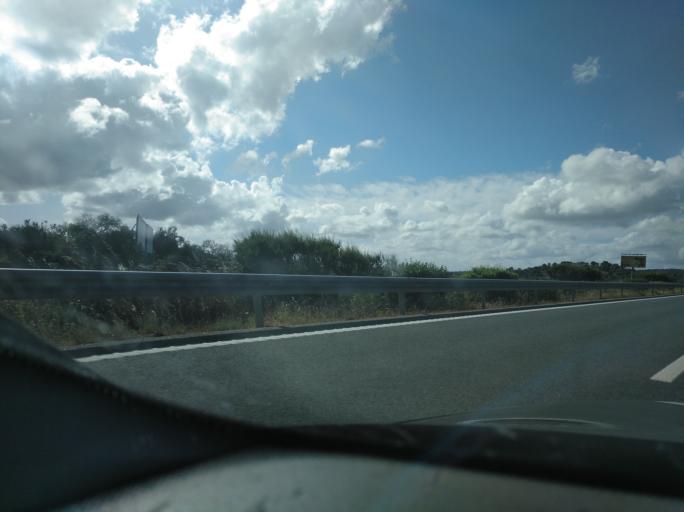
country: PT
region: Faro
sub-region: Silves
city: Sao Bartolomeu de Messines
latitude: 37.2186
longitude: -8.2420
